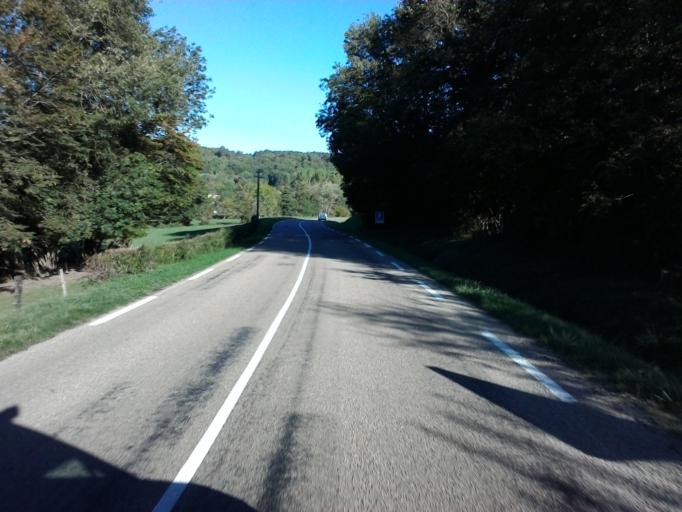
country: FR
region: Bourgogne
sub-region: Departement de la Cote-d'Or
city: Montbard
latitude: 47.6088
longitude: 4.3176
